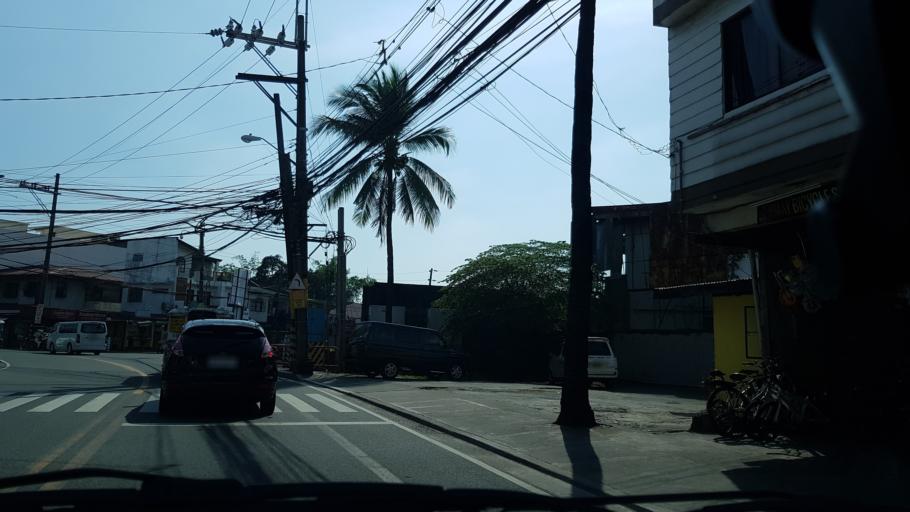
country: PH
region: Metro Manila
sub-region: Marikina
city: Calumpang
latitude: 14.6422
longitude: 121.0944
